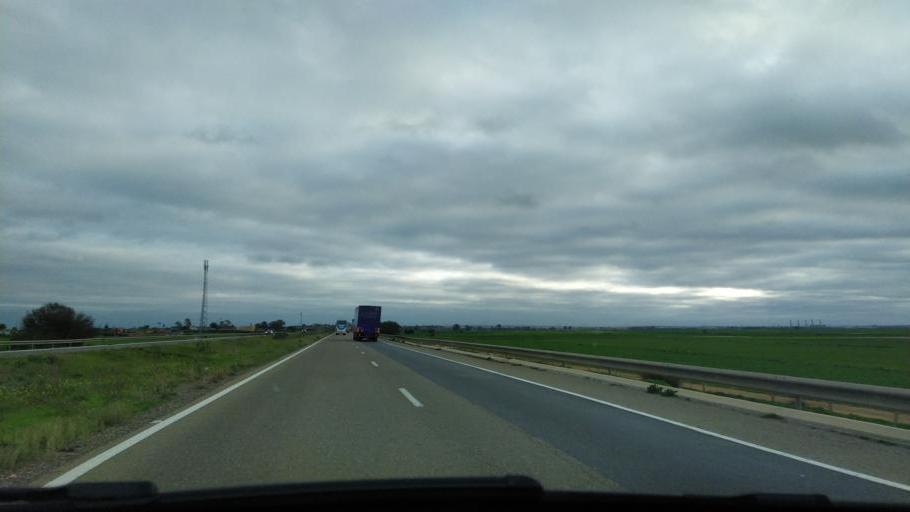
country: MA
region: Gharb-Chrarda-Beni Hssen
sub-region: Kenitra Province
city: Kenitra
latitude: 34.3287
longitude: -6.5104
